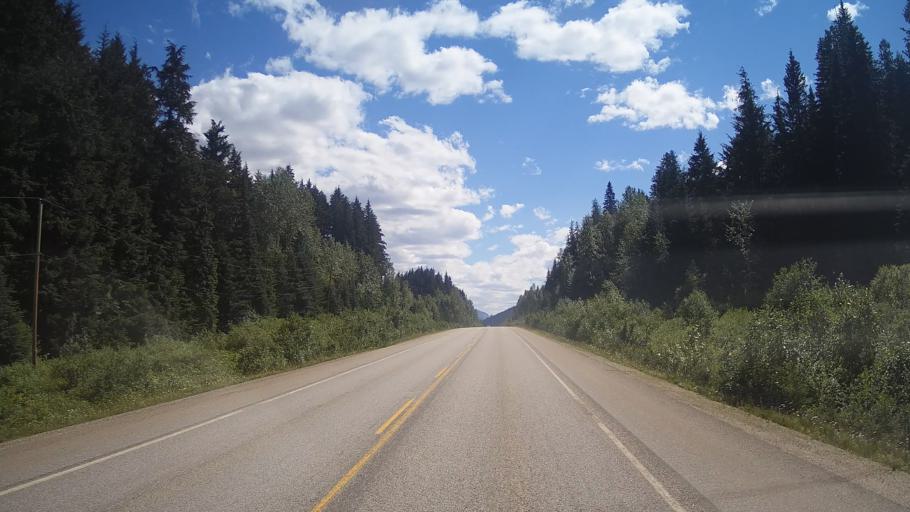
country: CA
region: Alberta
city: Jasper Park Lodge
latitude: 52.5557
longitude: -119.1112
